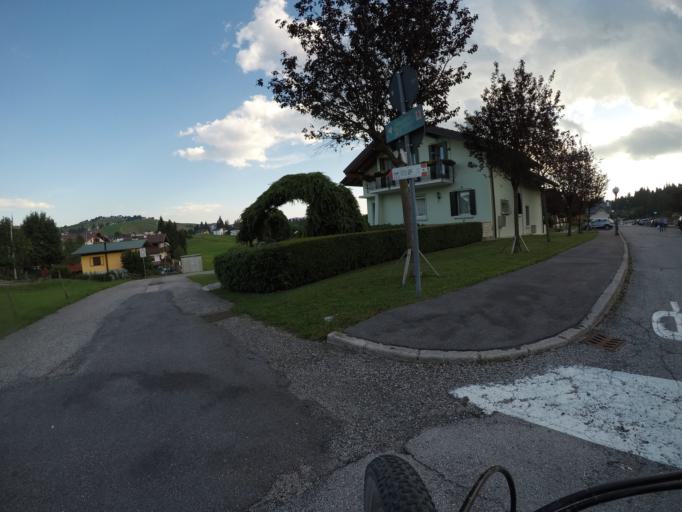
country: IT
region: Veneto
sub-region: Provincia di Vicenza
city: Gallio
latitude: 45.8910
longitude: 11.5456
